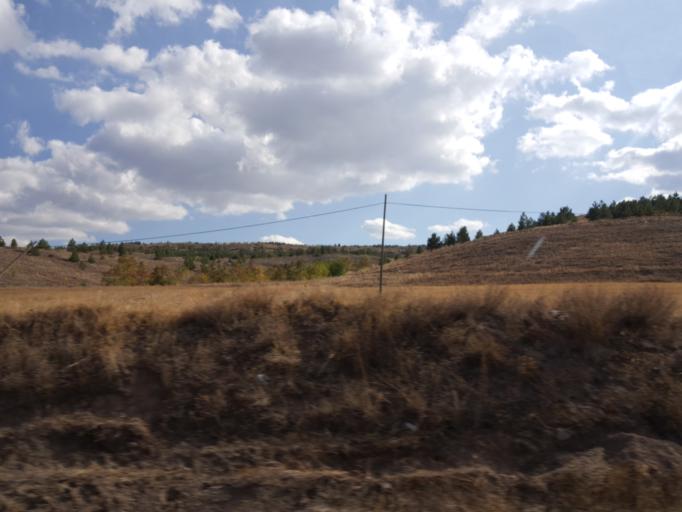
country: TR
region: Tokat
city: Sulusaray
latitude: 39.9892
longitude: 35.9980
